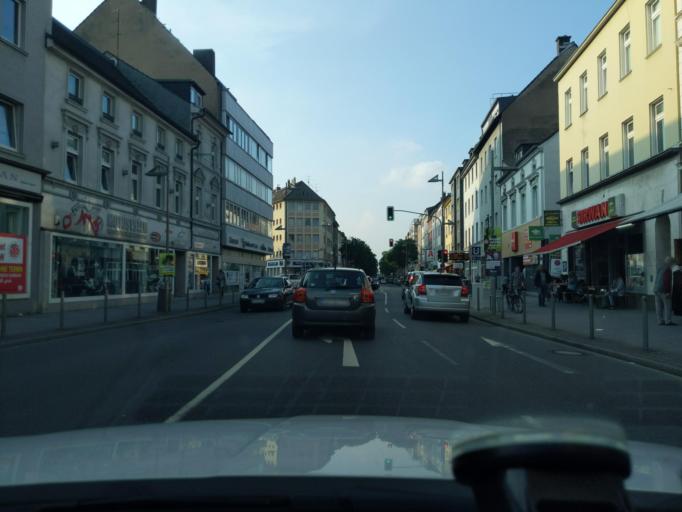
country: DE
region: North Rhine-Westphalia
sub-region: Regierungsbezirk Dusseldorf
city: Dusseldorf
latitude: 51.2124
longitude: 6.8066
